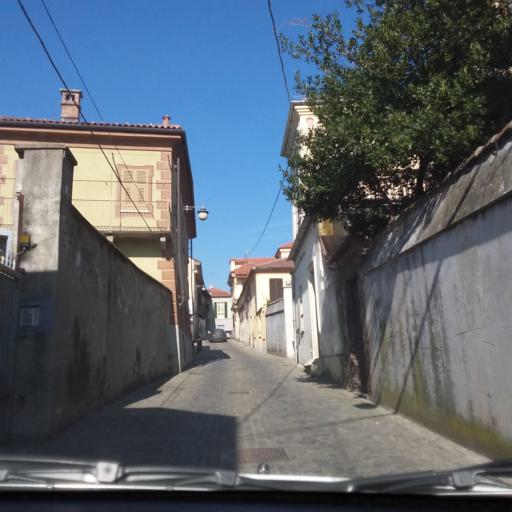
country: IT
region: Piedmont
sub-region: Provincia di Torino
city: Rivoli
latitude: 45.0705
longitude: 7.5154
